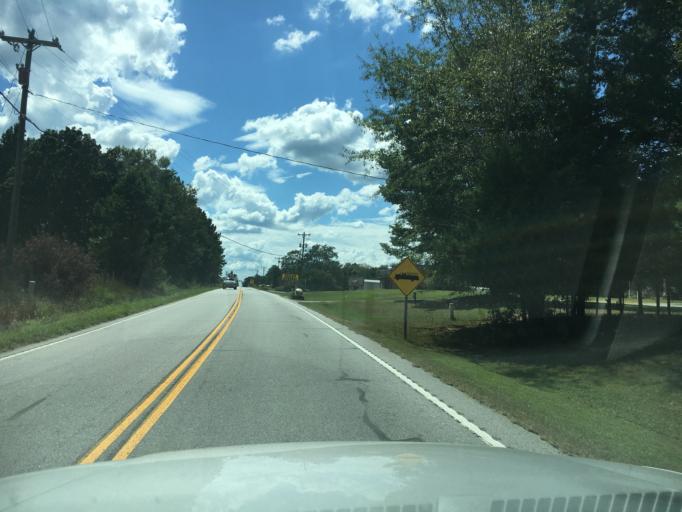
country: US
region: South Carolina
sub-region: Greenwood County
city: Ware Shoals
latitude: 34.5238
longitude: -82.1849
